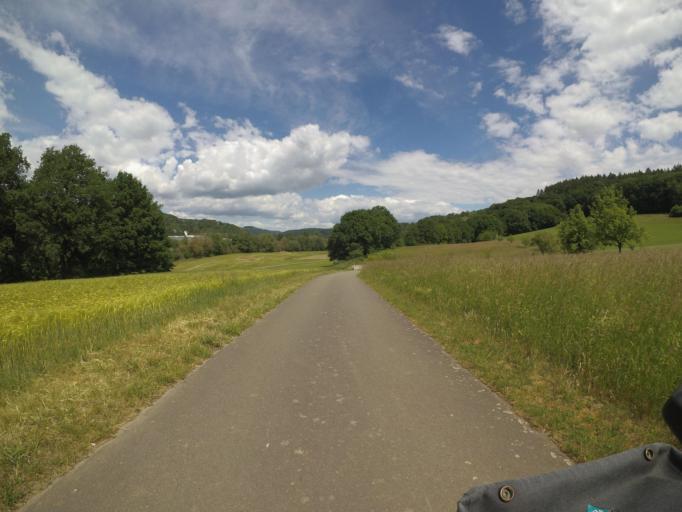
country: DE
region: Rheinland-Pfalz
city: Lauterecken
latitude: 49.6431
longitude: 7.5802
